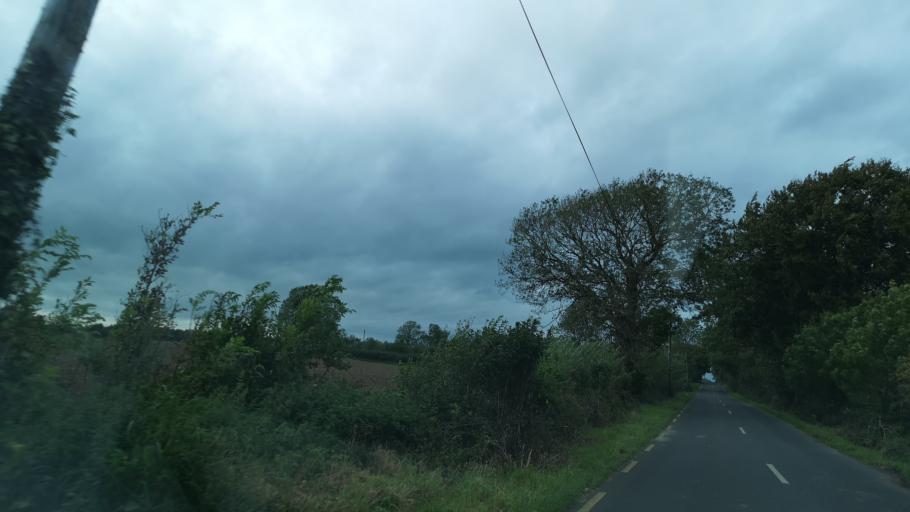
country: IE
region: Leinster
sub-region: Uibh Fhaili
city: Ferbane
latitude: 53.2009
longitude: -7.7820
